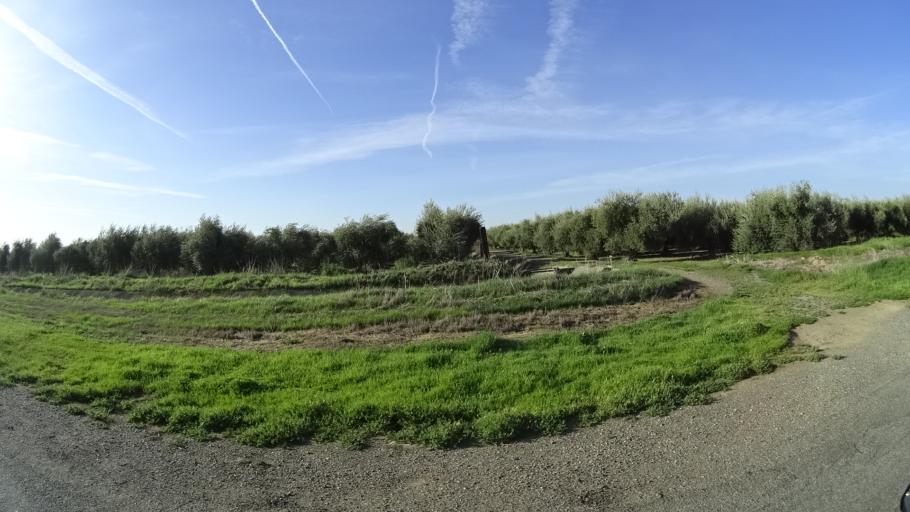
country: US
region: California
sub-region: Glenn County
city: Orland
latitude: 39.7332
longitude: -122.2203
